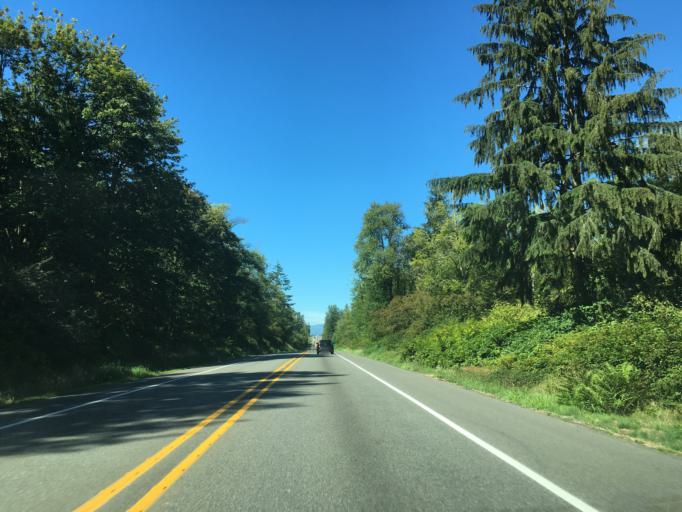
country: US
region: Washington
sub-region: Snohomish County
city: West Lake Stevens
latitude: 48.0429
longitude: -122.1107
